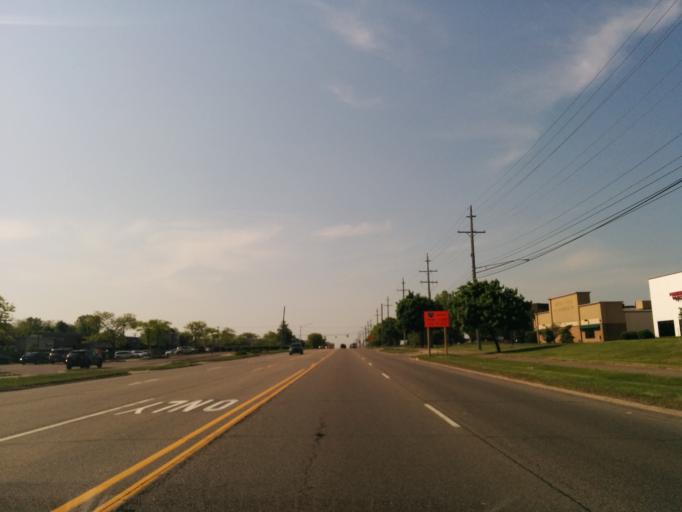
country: US
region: Michigan
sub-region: Oakland County
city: West Bloomfield Township
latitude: 42.5394
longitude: -83.3606
